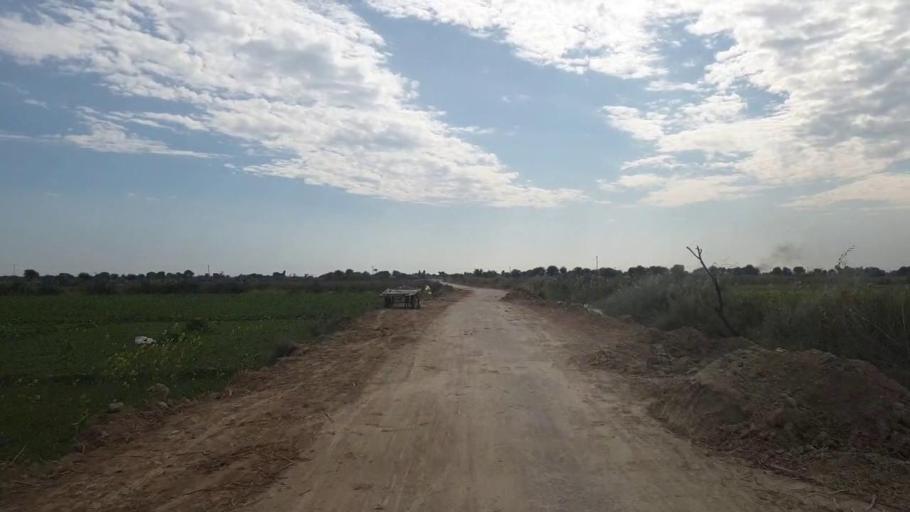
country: PK
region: Sindh
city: Jhol
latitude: 25.9990
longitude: 68.8957
